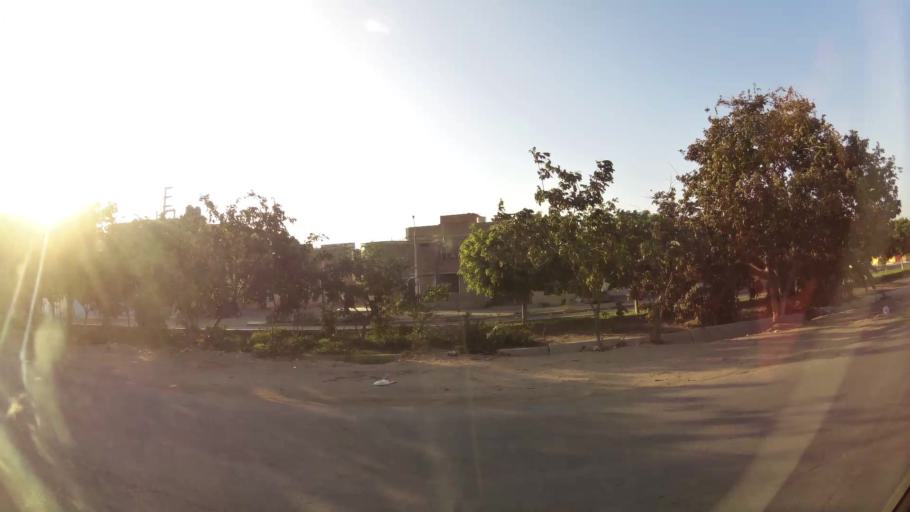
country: PE
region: Lambayeque
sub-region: Provincia de Chiclayo
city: Chiclayo
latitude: -6.7841
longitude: -79.8327
